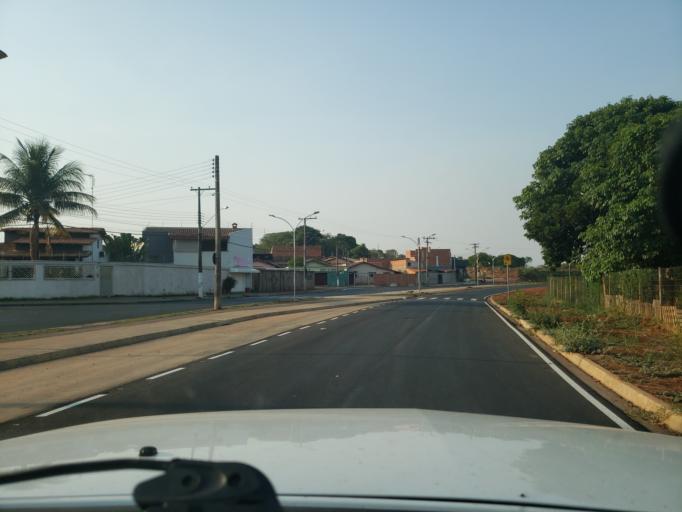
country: BR
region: Sao Paulo
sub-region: Moji-Guacu
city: Mogi-Gaucu
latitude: -22.3270
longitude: -46.9506
